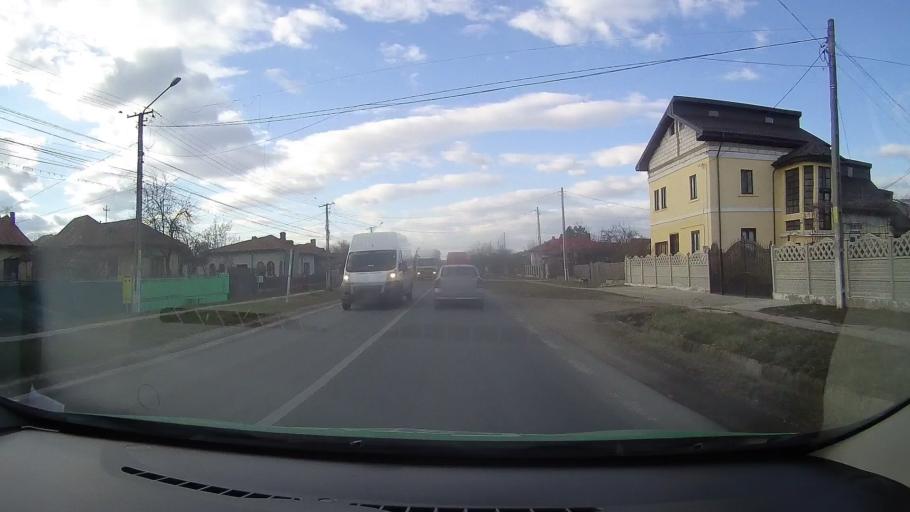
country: RO
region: Dambovita
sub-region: Comuna Ulmi
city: Ulmi
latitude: 44.8925
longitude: 25.5044
